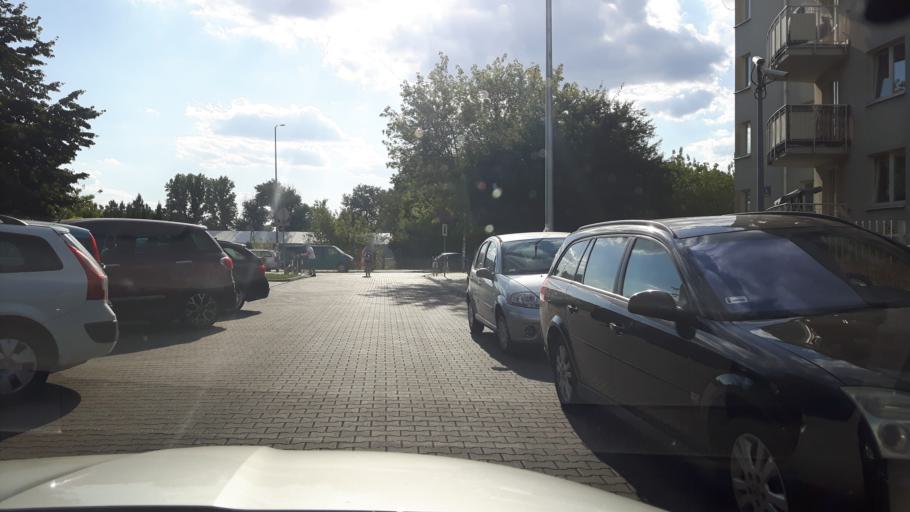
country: PL
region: Masovian Voivodeship
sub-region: Warszawa
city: Targowek
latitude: 52.2882
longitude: 21.0533
